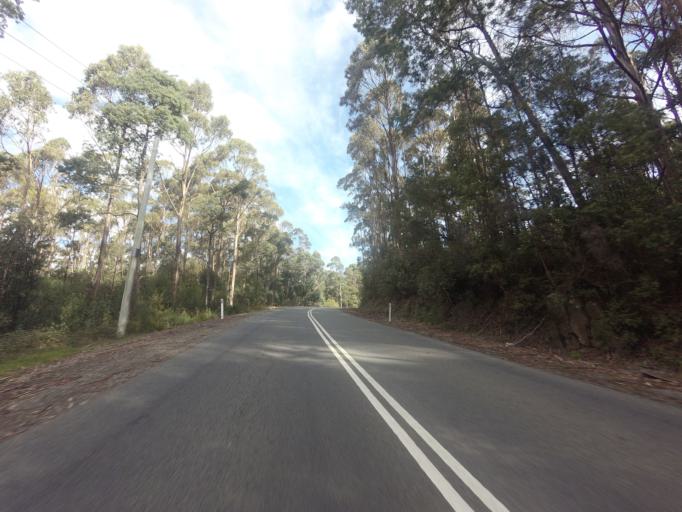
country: AU
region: Tasmania
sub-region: Clarence
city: Sandford
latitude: -43.1397
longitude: 147.8253
